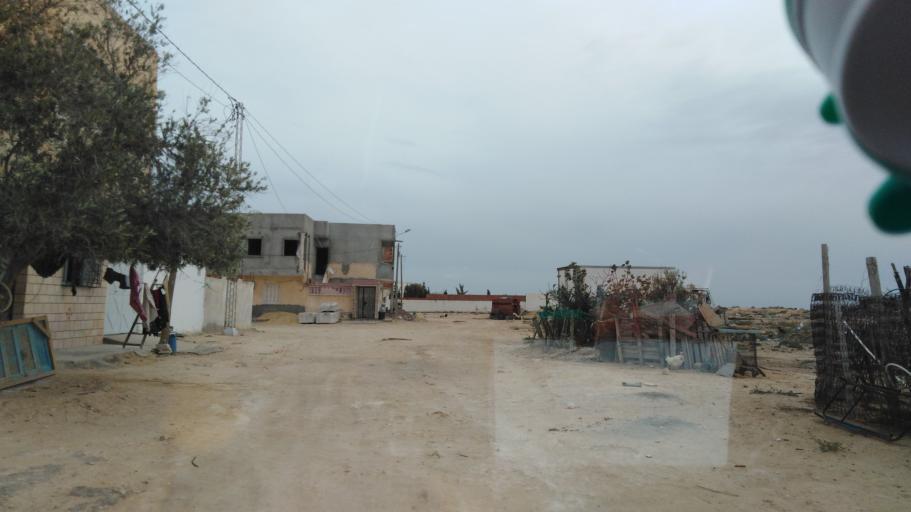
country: TN
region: Qabis
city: Gabes
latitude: 33.9487
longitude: 10.0026
